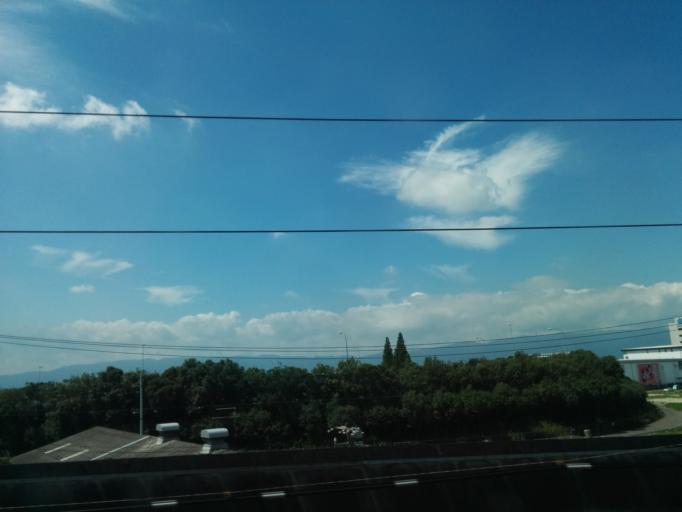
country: JP
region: Aichi
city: Sobue
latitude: 35.3091
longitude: 136.6935
